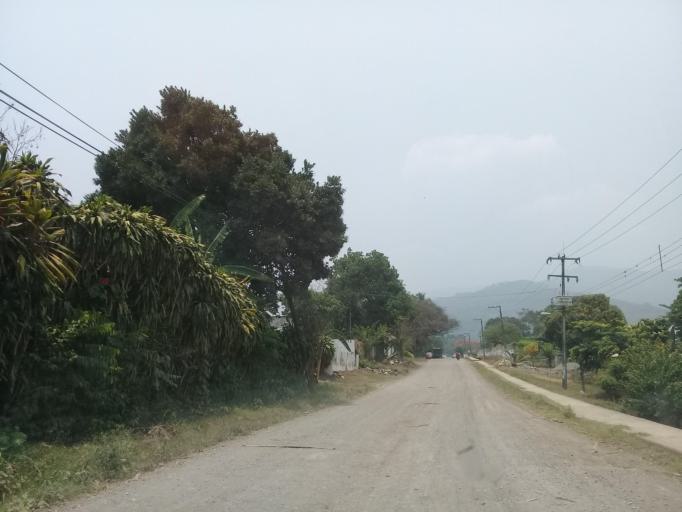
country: MX
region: Veracruz
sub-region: Tezonapa
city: Laguna Chica (Pueblo Nuevo)
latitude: 18.5402
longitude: -96.7332
